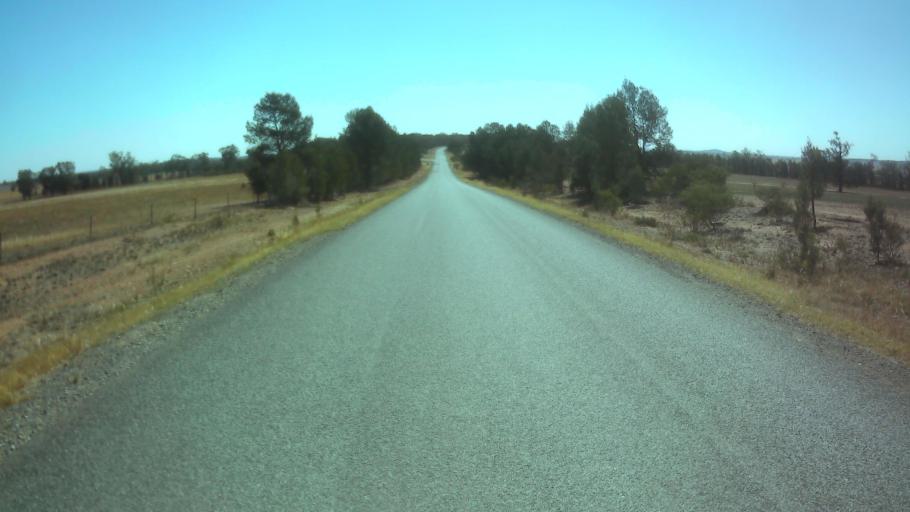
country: AU
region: New South Wales
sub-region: Weddin
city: Grenfell
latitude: -33.7546
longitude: 147.8348
